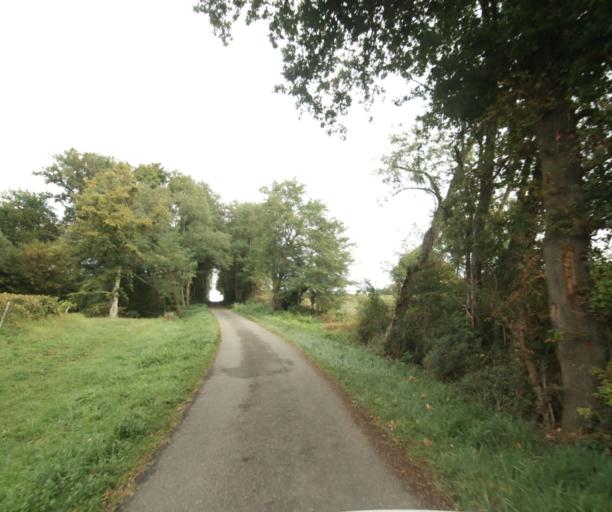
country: FR
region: Midi-Pyrenees
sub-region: Departement du Gers
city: Nogaro
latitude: 43.8293
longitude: -0.0726
